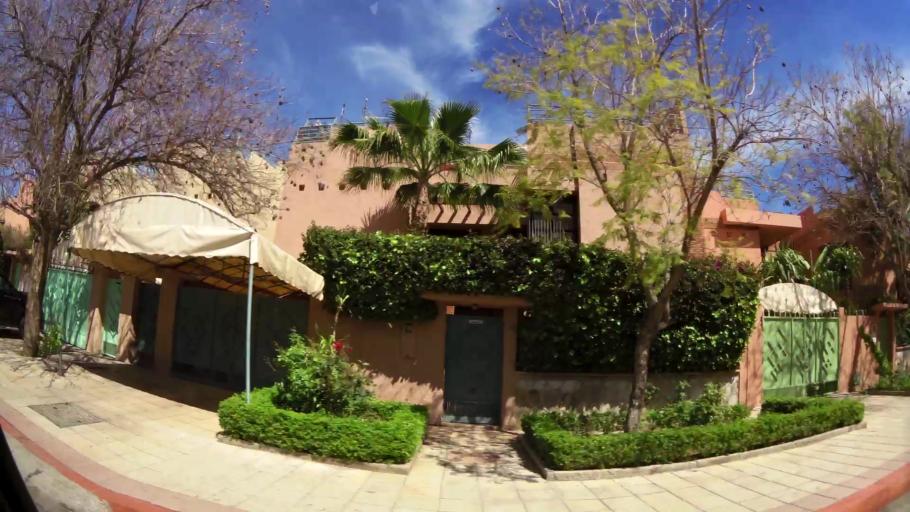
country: MA
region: Marrakech-Tensift-Al Haouz
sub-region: Marrakech
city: Marrakesh
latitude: 31.6676
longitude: -8.0085
